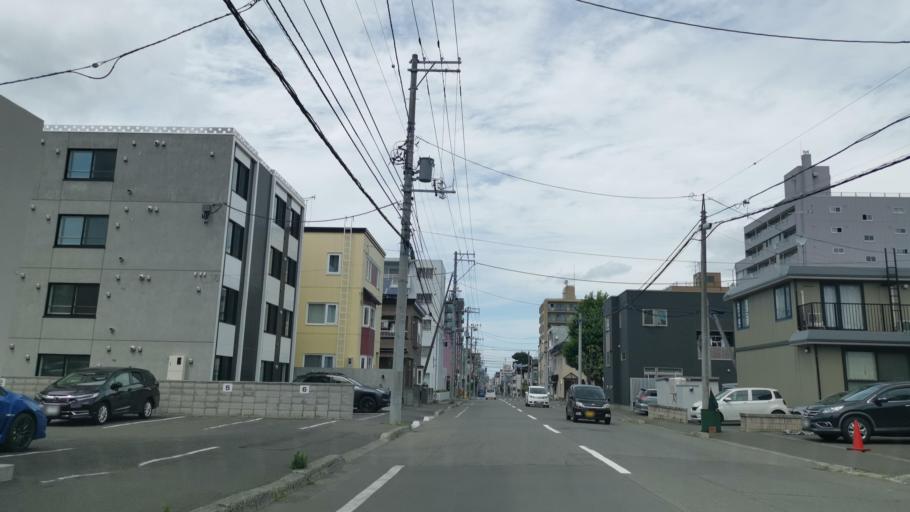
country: JP
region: Hokkaido
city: Sapporo
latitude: 43.0298
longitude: 141.3485
